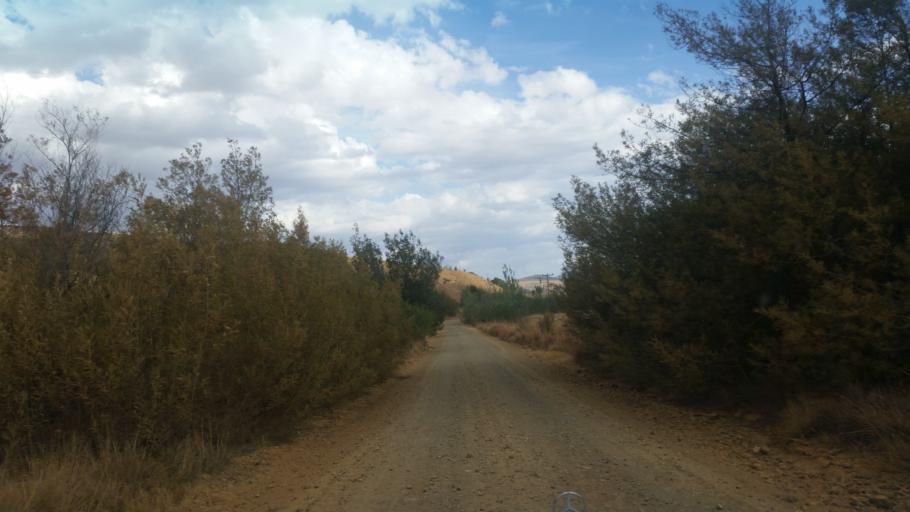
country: ZA
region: Orange Free State
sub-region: Thabo Mofutsanyana District Municipality
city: Phuthaditjhaba
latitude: -28.3397
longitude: 28.6127
